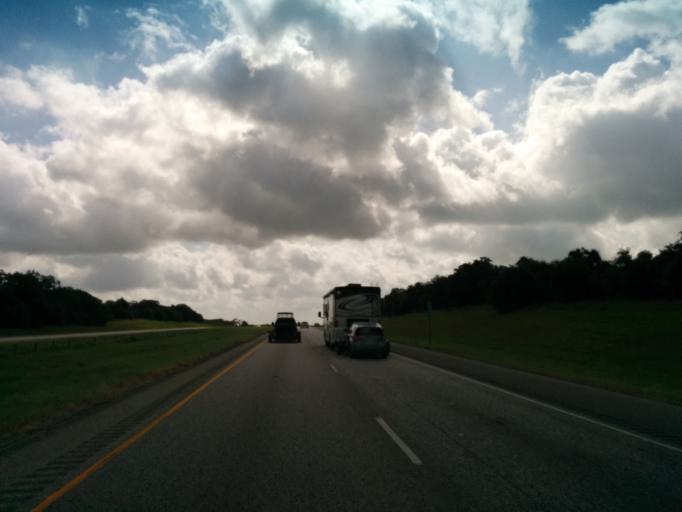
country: US
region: Texas
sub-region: Gonzales County
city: Waelder
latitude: 29.6603
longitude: -97.3991
